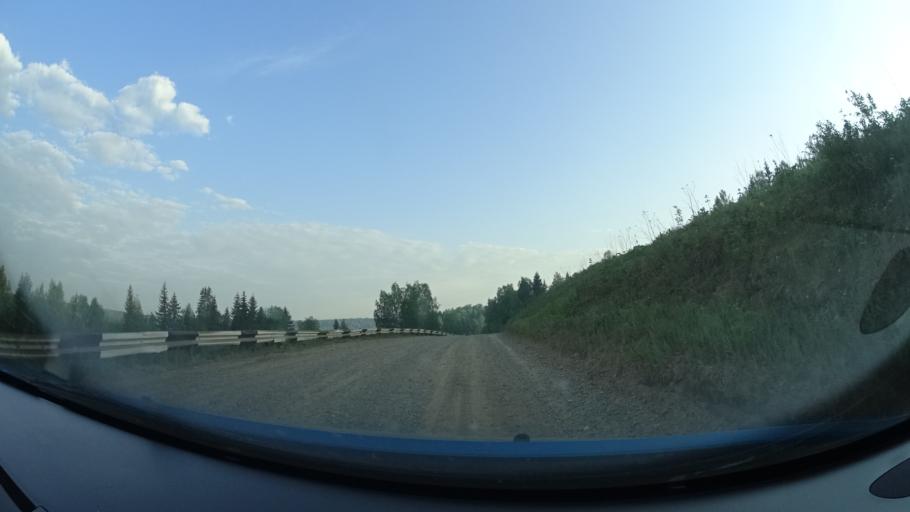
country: RU
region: Perm
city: Kuyeda
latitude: 56.6476
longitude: 55.7006
